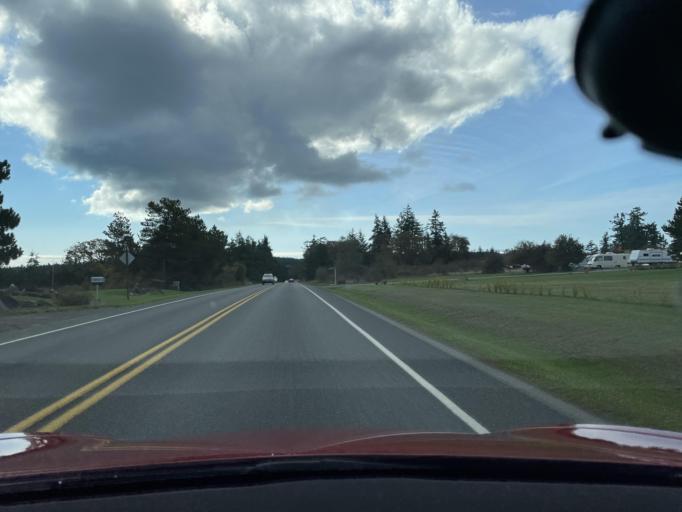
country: US
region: Washington
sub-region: San Juan County
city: Friday Harbor
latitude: 48.5093
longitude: -123.0363
